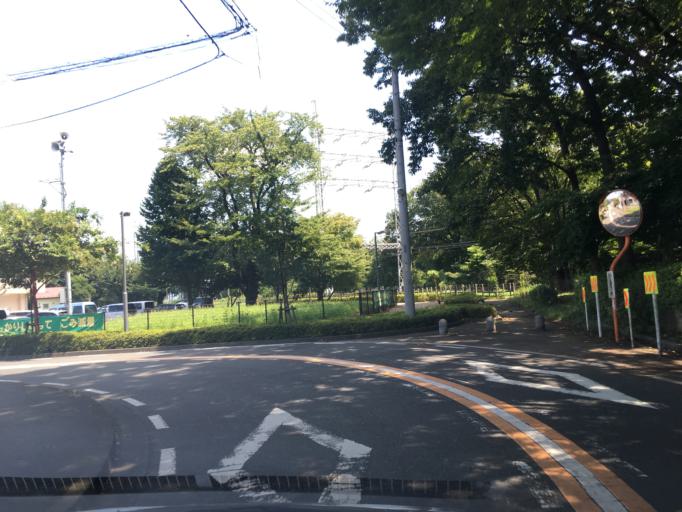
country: JP
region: Tokyo
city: Fussa
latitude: 35.7213
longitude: 139.3525
